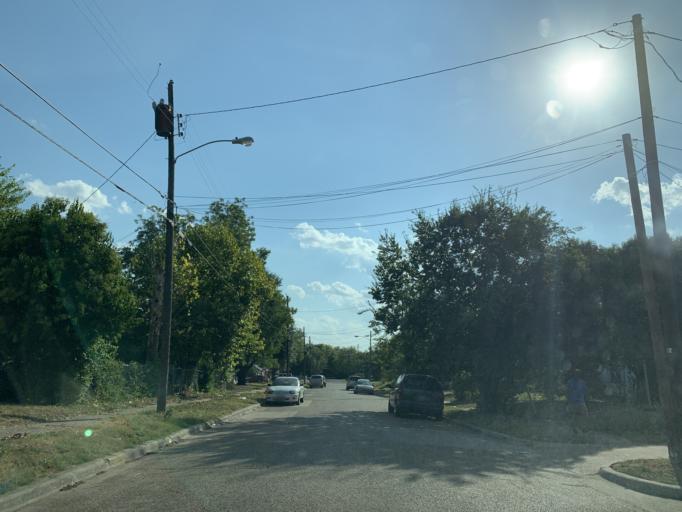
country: US
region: Texas
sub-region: Dallas County
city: Hutchins
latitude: 32.6954
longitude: -96.7798
